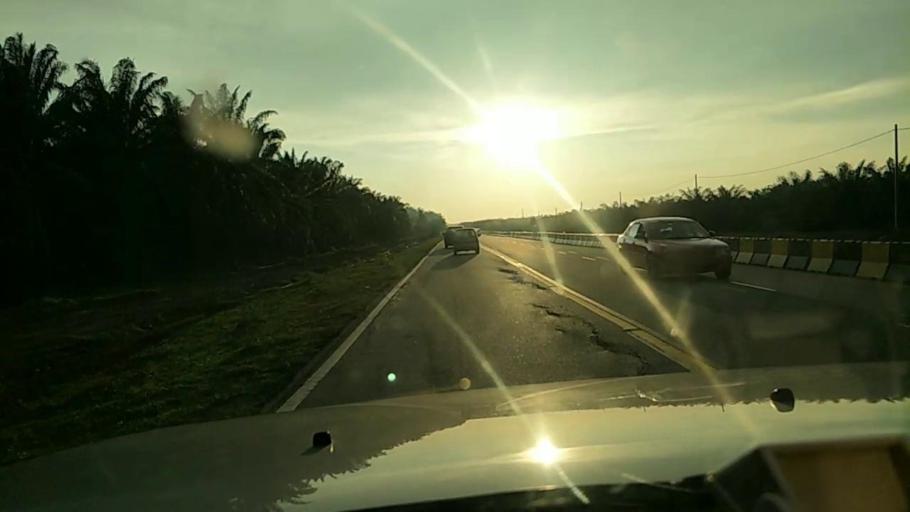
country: MY
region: Perak
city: Kampong Dungun
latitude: 3.3071
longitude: 101.3397
